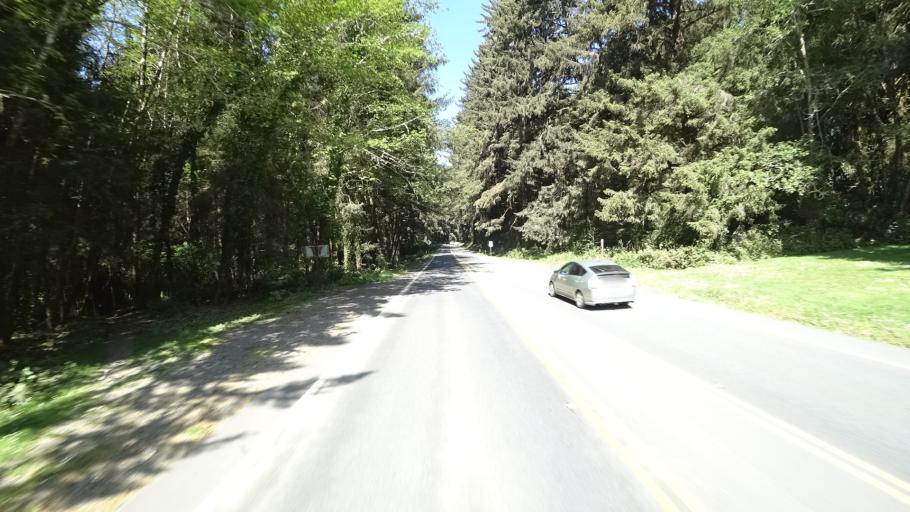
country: US
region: California
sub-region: Del Norte County
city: Bertsch-Oceanview
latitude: 41.5844
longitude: -124.0881
